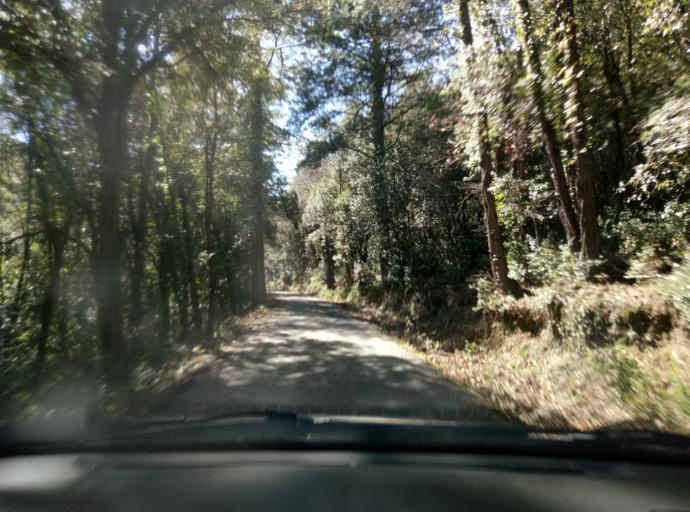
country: ES
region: Catalonia
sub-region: Provincia de Tarragona
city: Capafonts
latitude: 41.3411
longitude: 1.0568
